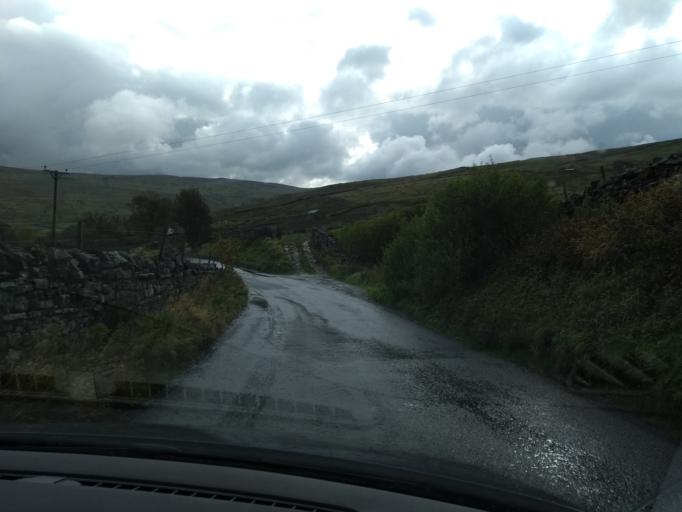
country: GB
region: England
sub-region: Cumbria
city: Kirkby Stephen
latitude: 54.3886
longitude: -2.1739
